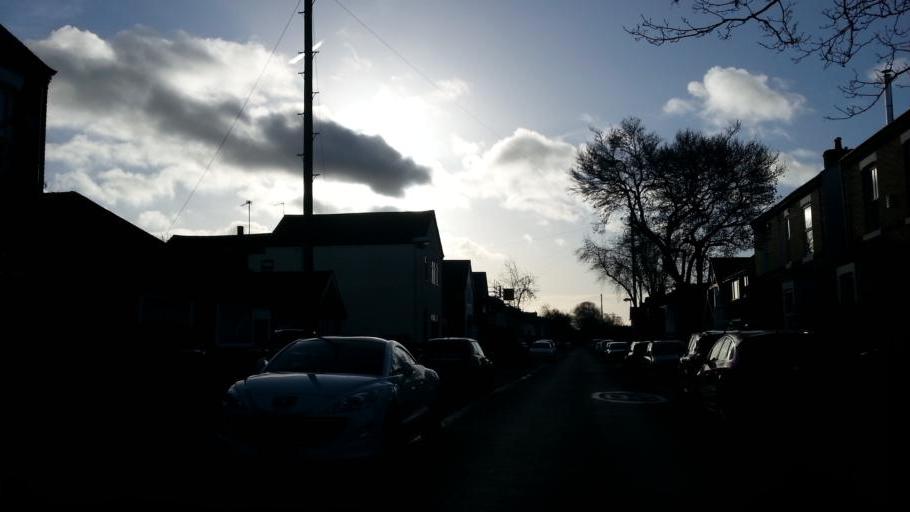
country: GB
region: England
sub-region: Nottinghamshire
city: West Bridgford
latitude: 52.9367
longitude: -1.1167
